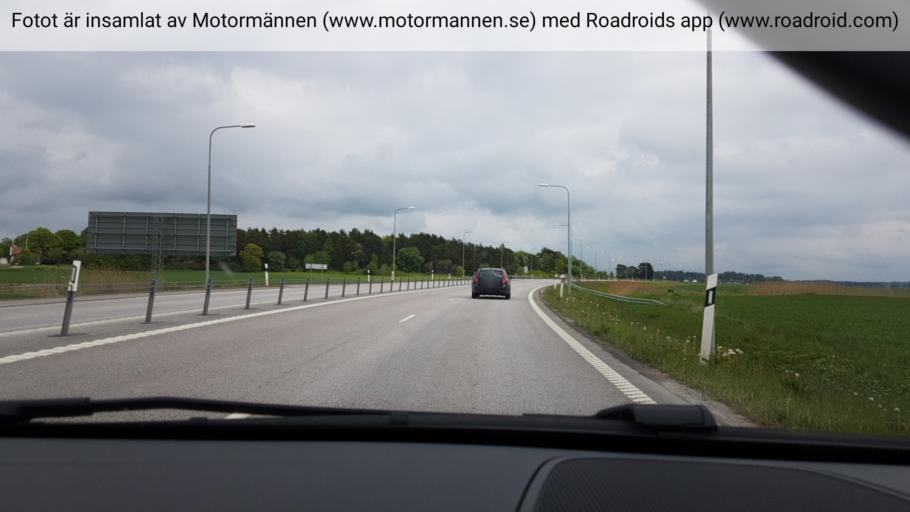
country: SE
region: Uppsala
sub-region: Uppsala Kommun
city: Gamla Uppsala
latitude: 59.8896
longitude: 17.6743
